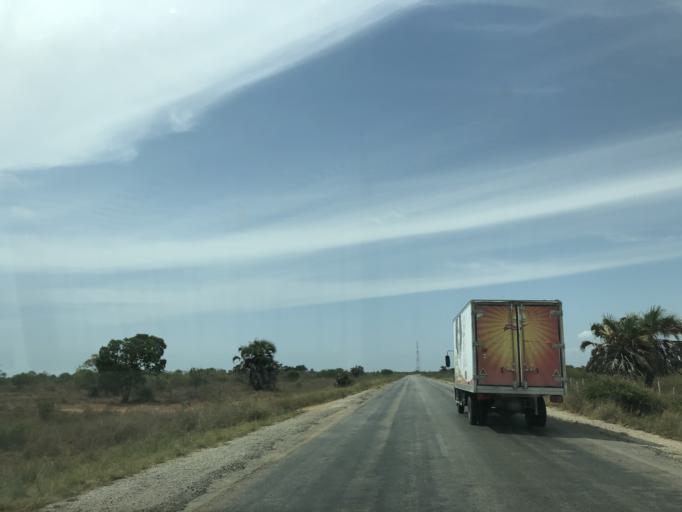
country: AO
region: Cuanza Sul
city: Sumbe
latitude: -10.5821
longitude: 13.7522
